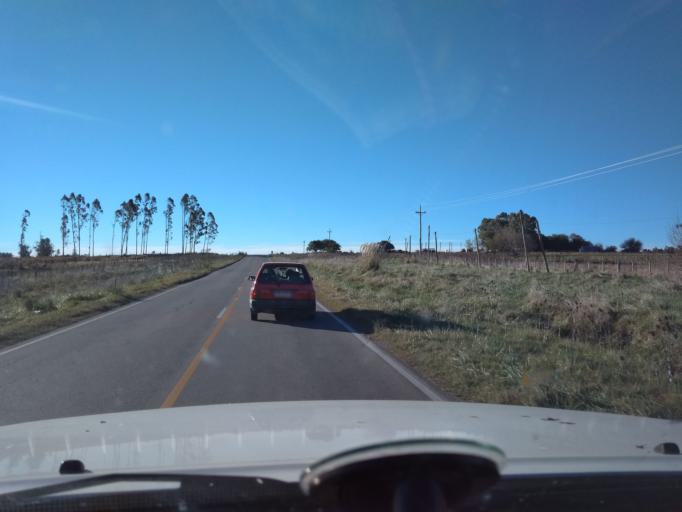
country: UY
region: Canelones
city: San Ramon
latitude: -34.3531
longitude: -55.9595
